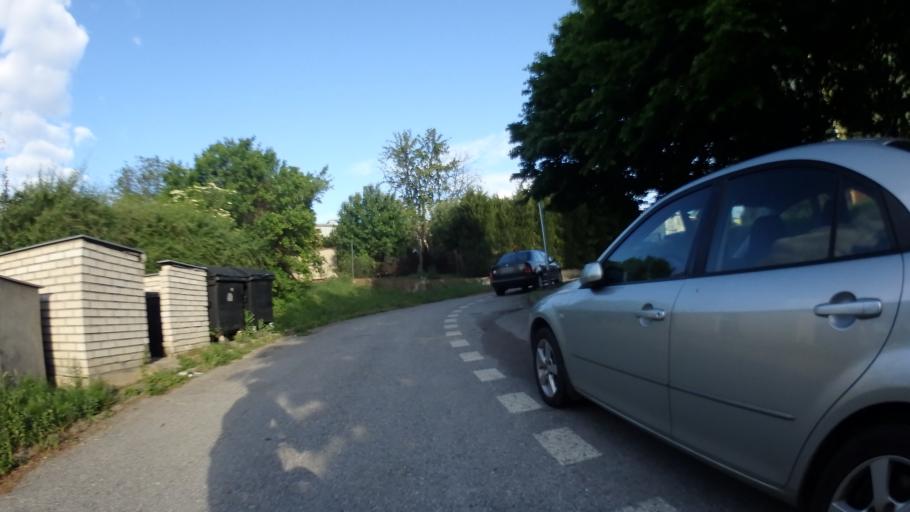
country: CZ
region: South Moravian
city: Ostopovice
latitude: 49.1622
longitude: 16.5485
